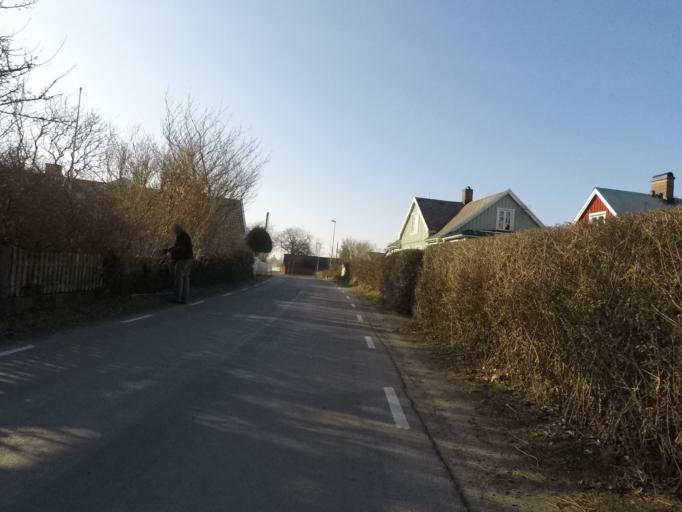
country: SE
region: Skane
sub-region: Hoganas Kommun
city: Hoganas
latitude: 56.2438
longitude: 12.6451
